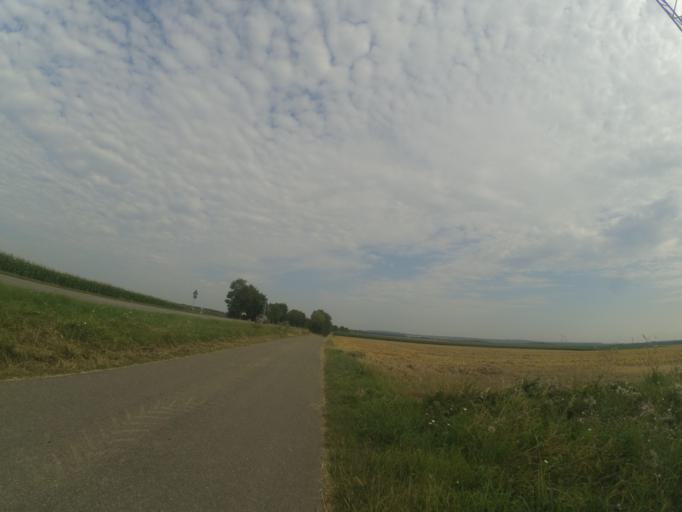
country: DE
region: Baden-Wuerttemberg
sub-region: Tuebingen Region
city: Dornstadt
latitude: 48.4908
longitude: 9.9311
